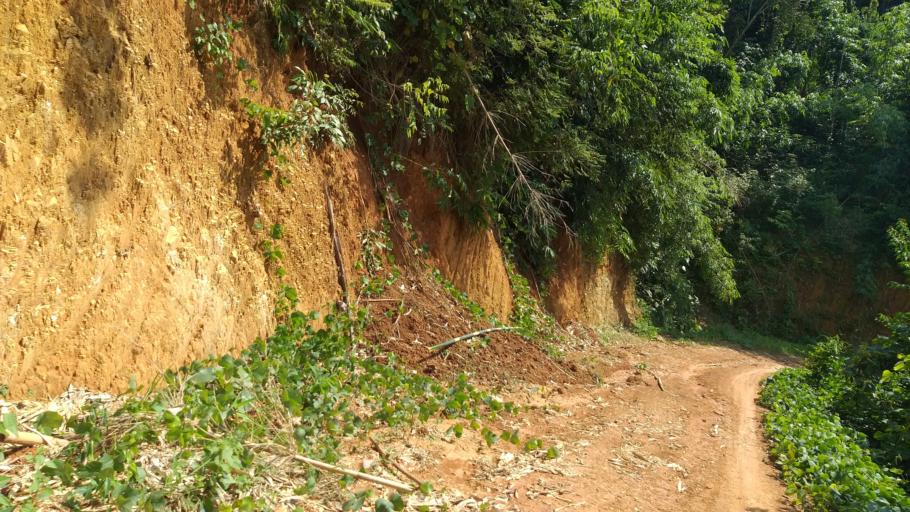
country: LA
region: Phongsali
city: Khoa
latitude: 21.2708
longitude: 102.5164
